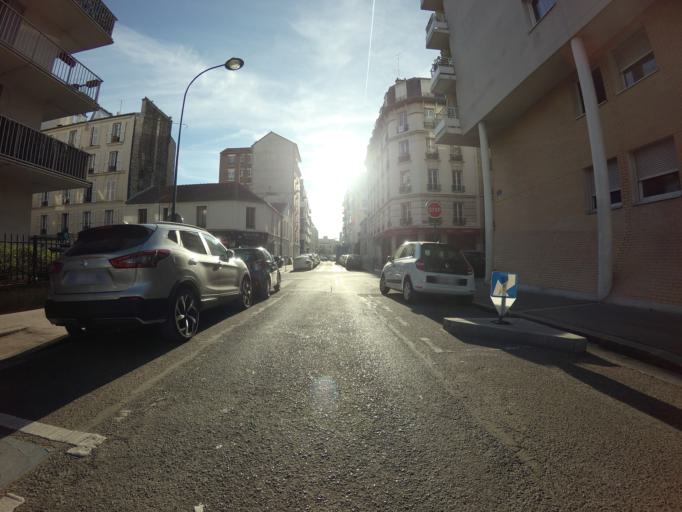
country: FR
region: Ile-de-France
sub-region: Departement des Hauts-de-Seine
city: Clichy
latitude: 48.9008
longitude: 2.3144
